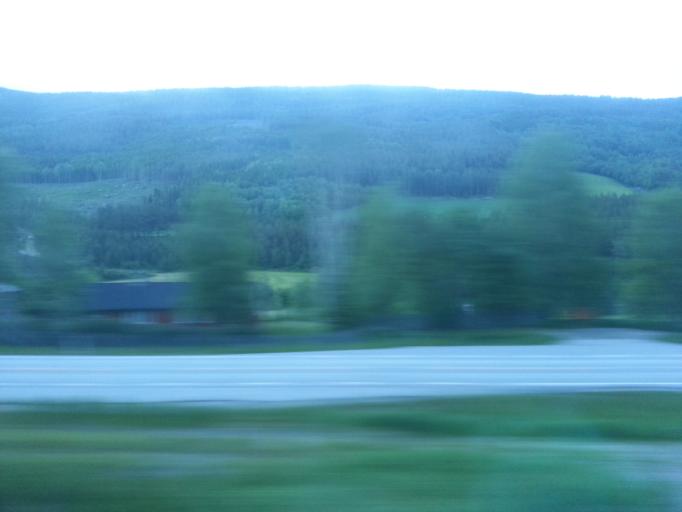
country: NO
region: Oppland
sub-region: Dovre
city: Dovre
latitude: 61.9025
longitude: 9.3708
